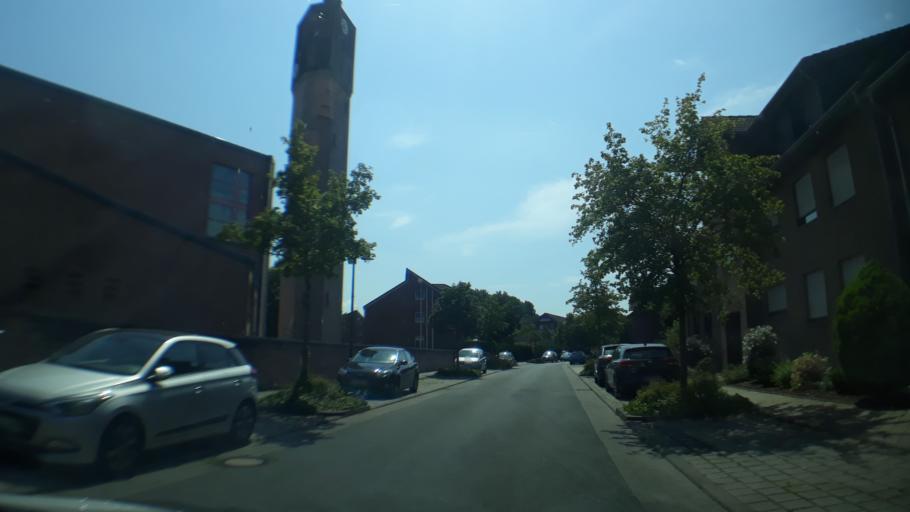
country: DE
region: North Rhine-Westphalia
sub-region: Regierungsbezirk Koln
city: Langerwehe
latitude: 50.8421
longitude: 6.3571
